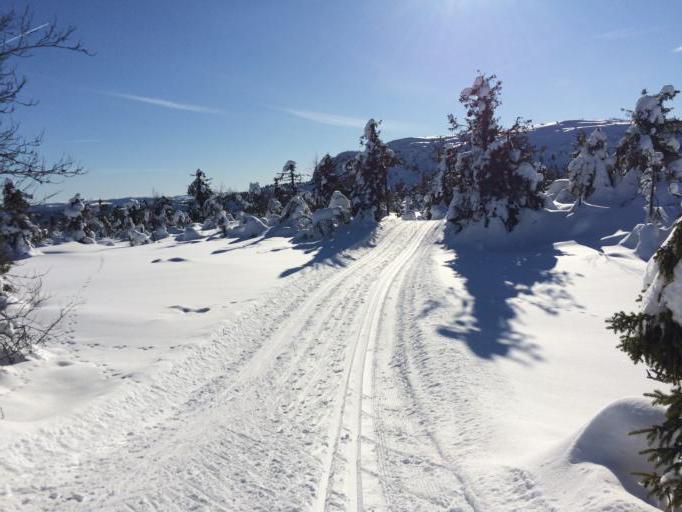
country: NO
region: Oppland
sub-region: Gausdal
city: Segalstad bru
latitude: 61.3094
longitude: 10.1034
